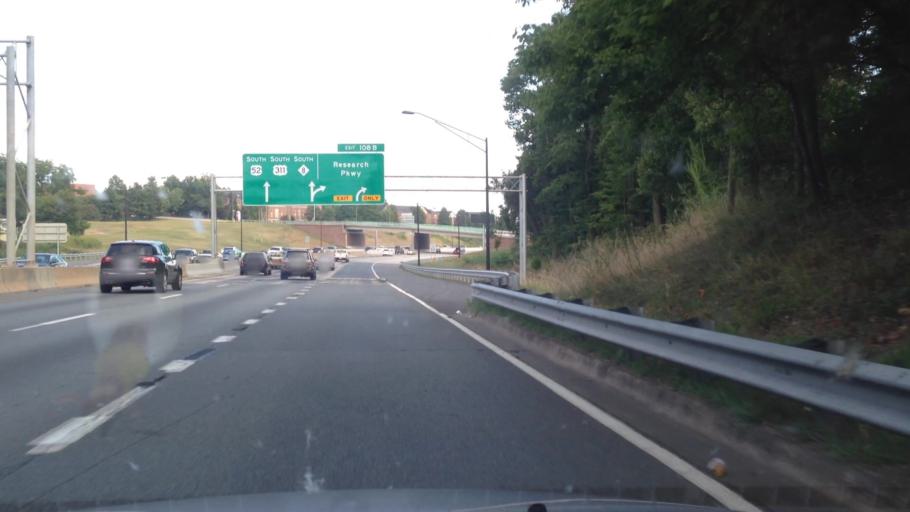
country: US
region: North Carolina
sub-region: Forsyth County
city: Winston-Salem
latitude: 36.0927
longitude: -80.2314
